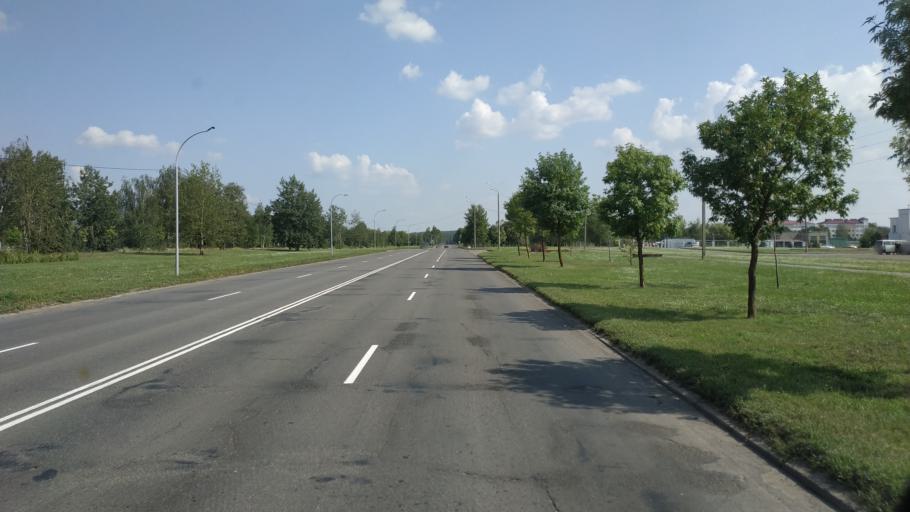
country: BY
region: Mogilev
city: Buynichy
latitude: 53.8609
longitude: 30.3237
